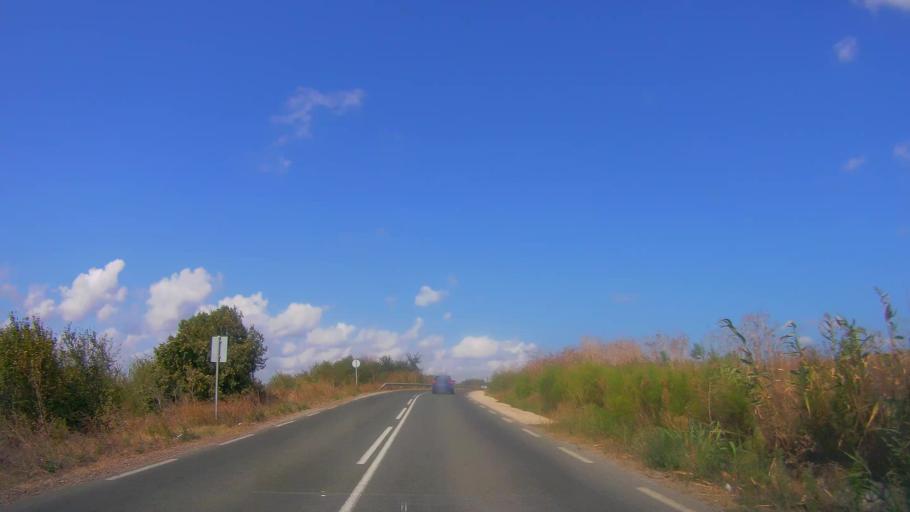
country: BG
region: Burgas
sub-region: Obshtina Burgas
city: Burgas
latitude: 42.4795
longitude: 27.3728
